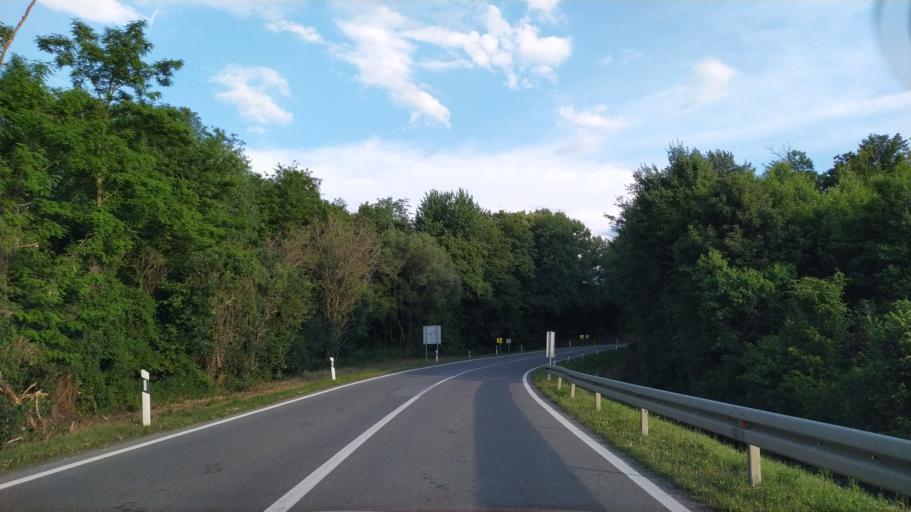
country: HR
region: Osjecko-Baranjska
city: Fericanci
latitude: 45.5137
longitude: 18.0108
